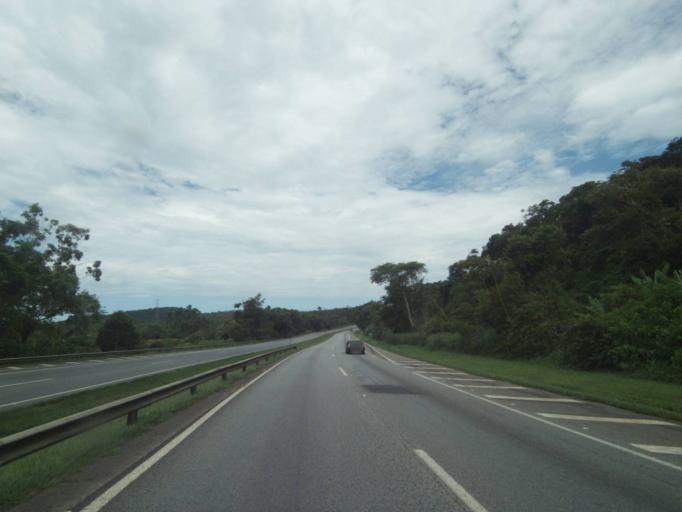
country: BR
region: Parana
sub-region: Antonina
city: Antonina
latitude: -25.5294
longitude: -48.7239
